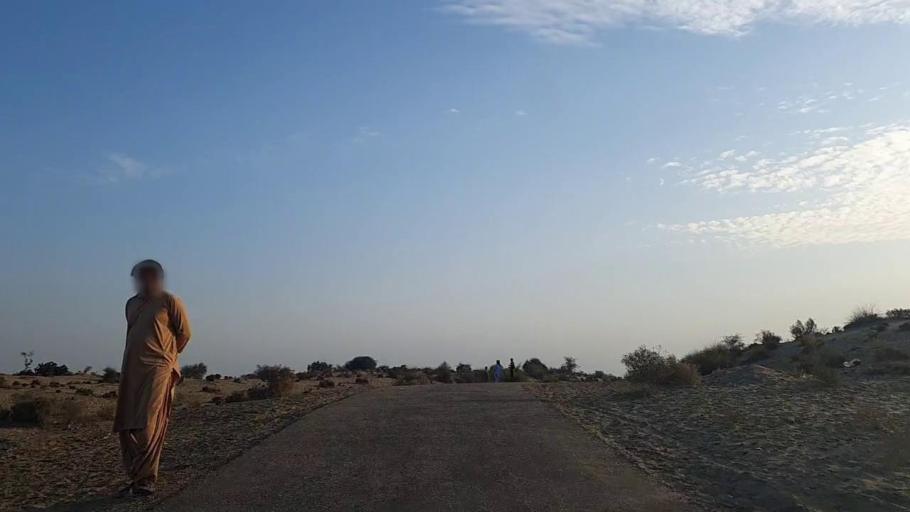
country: PK
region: Sindh
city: Jam Sahib
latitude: 26.3963
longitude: 68.5010
